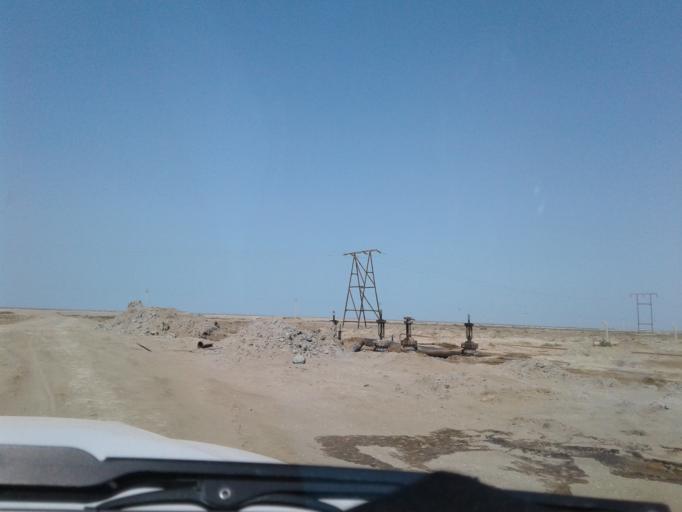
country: IR
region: Golestan
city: Gomishan
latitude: 37.8196
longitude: 53.9217
